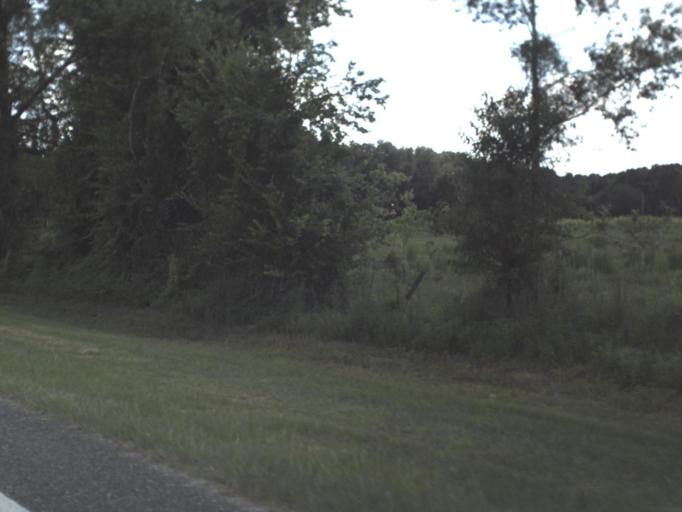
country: US
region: Florida
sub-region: Alachua County
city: High Springs
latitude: 29.8965
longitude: -82.6093
